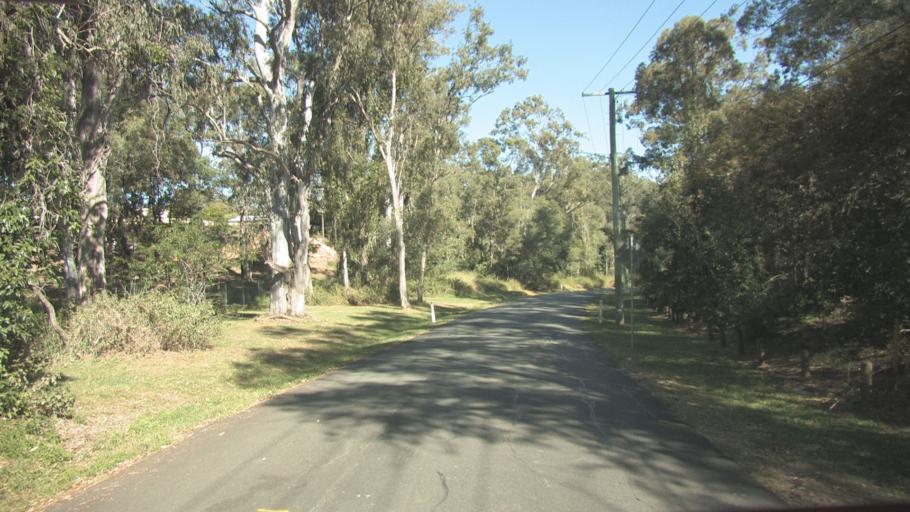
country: AU
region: Queensland
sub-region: Logan
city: Slacks Creek
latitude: -27.6586
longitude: 153.1631
